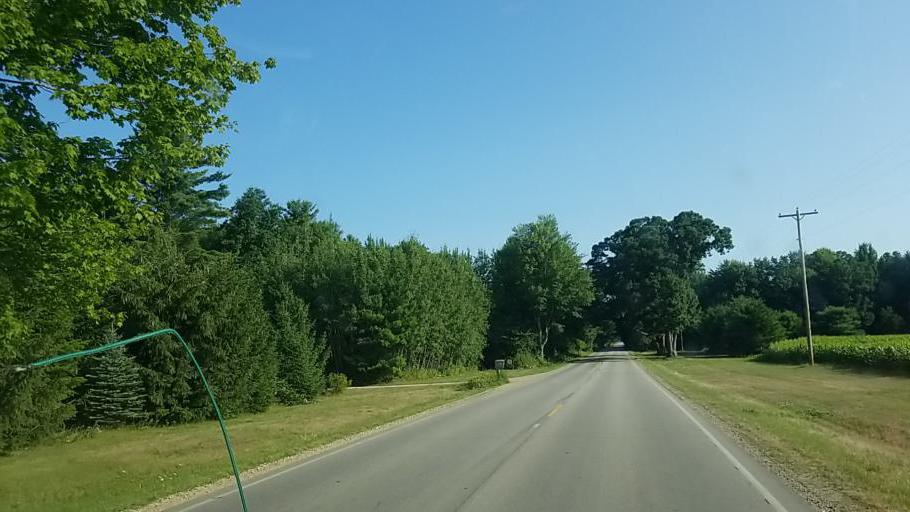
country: US
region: Michigan
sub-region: Newaygo County
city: Fremont
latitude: 43.3677
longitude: -85.9395
